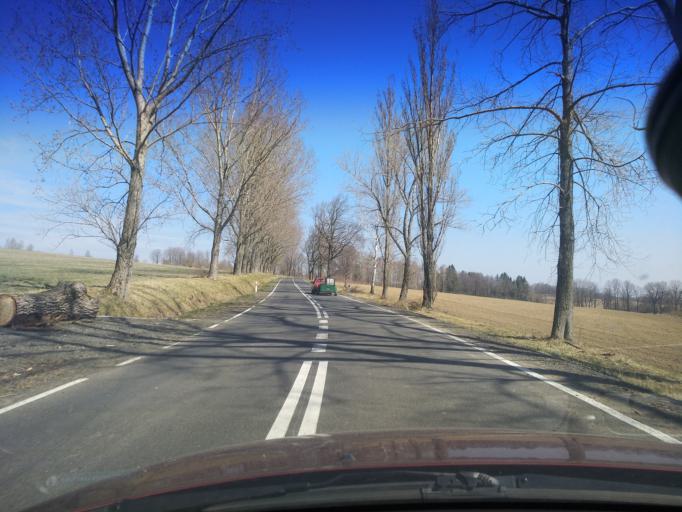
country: PL
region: Lower Silesian Voivodeship
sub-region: Powiat lubanski
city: Lesna
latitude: 50.9833
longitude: 15.3179
